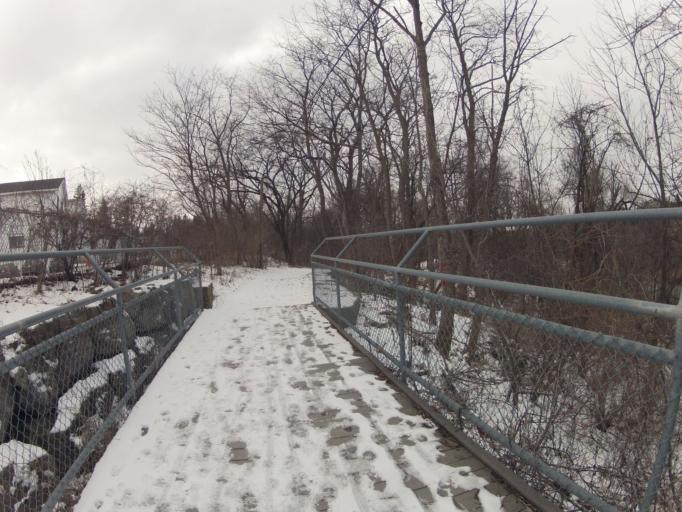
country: CA
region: Ontario
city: Mississauga
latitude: 43.5744
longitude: -79.6946
